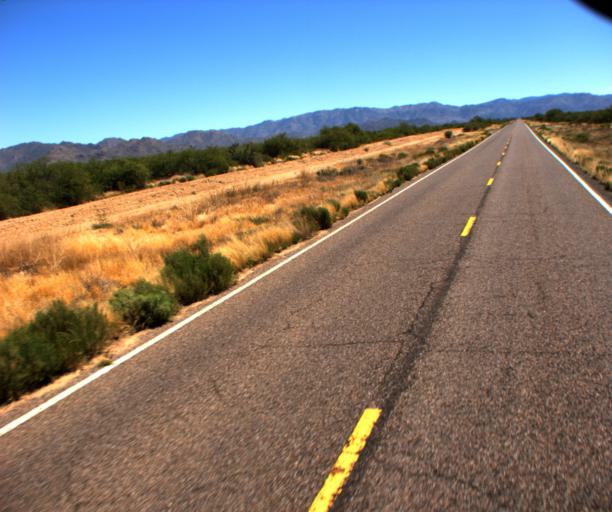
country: US
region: Arizona
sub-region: Yavapai County
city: Congress
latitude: 34.1280
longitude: -112.9391
